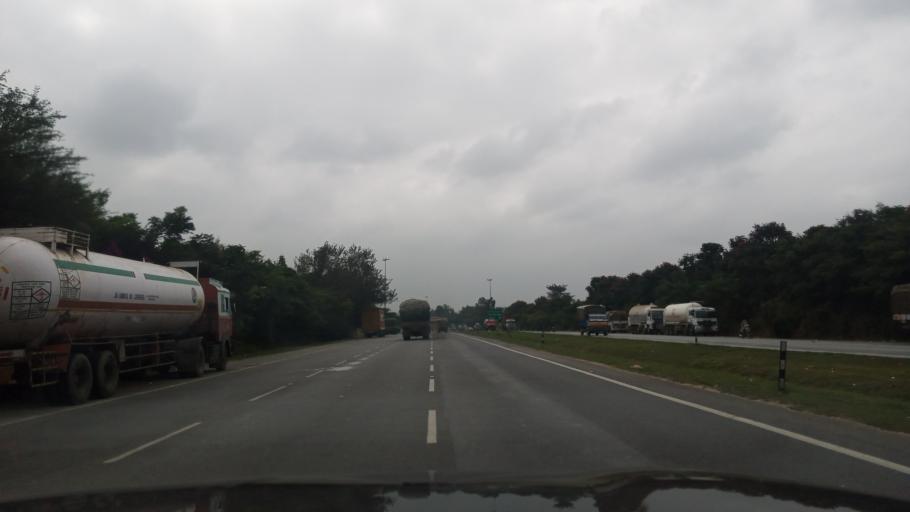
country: IN
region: Karnataka
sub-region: Bangalore Rural
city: Nelamangala
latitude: 13.0476
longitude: 77.4759
